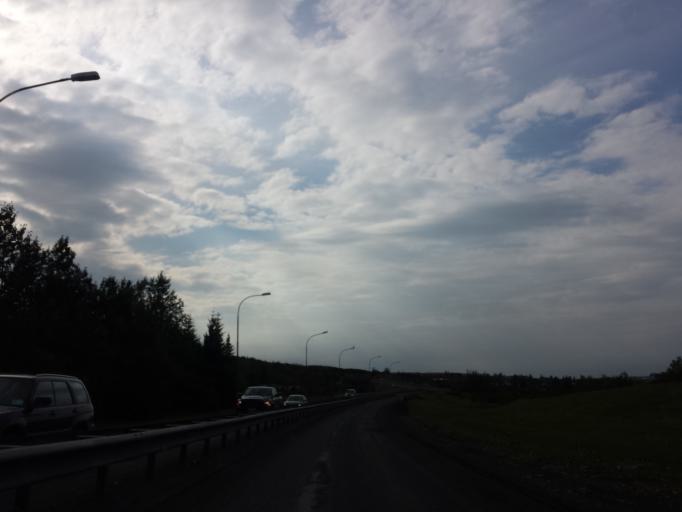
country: IS
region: Capital Region
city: Reykjavik
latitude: 64.1174
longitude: -21.8157
